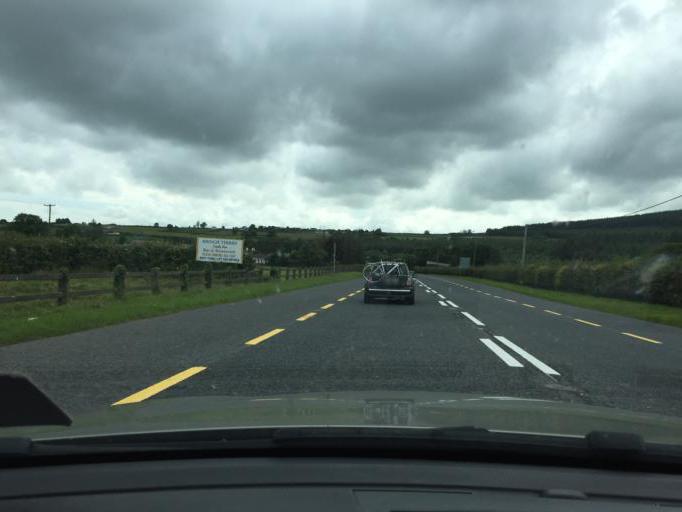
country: IE
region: Munster
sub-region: Waterford
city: Dungarvan
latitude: 52.1383
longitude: -7.5568
